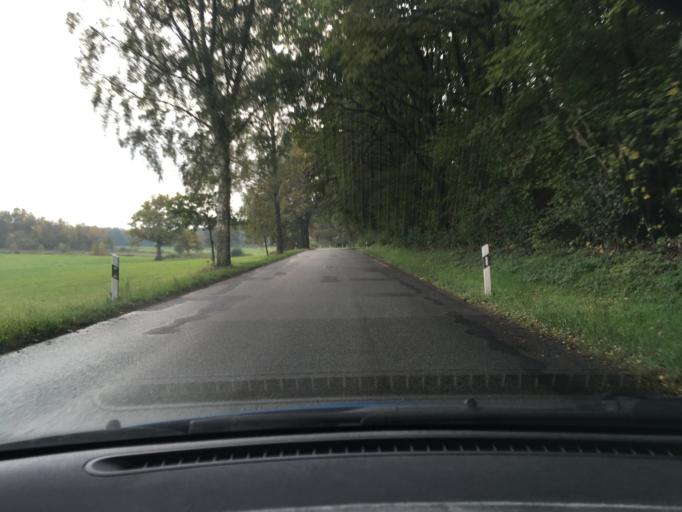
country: DE
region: Schleswig-Holstein
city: Tensfeld
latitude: 54.0344
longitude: 10.3101
